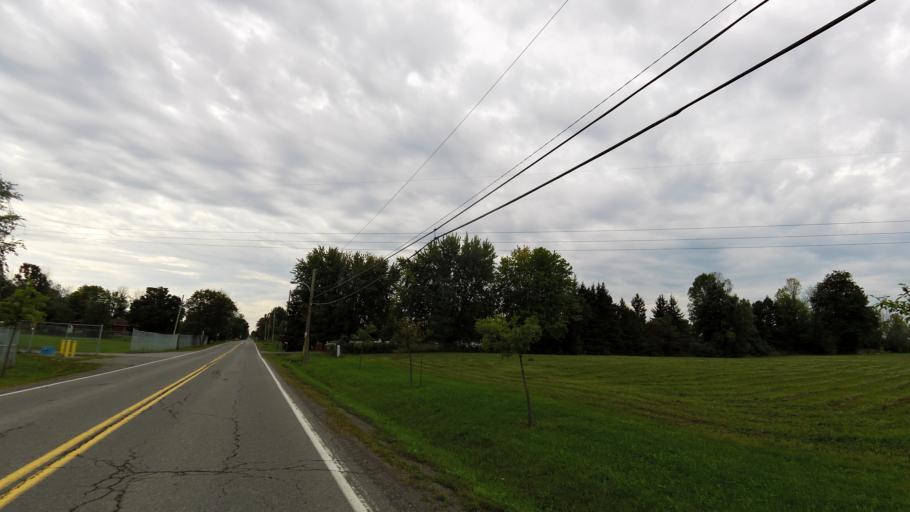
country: CA
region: Ontario
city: Ottawa
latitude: 45.2277
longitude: -75.4685
